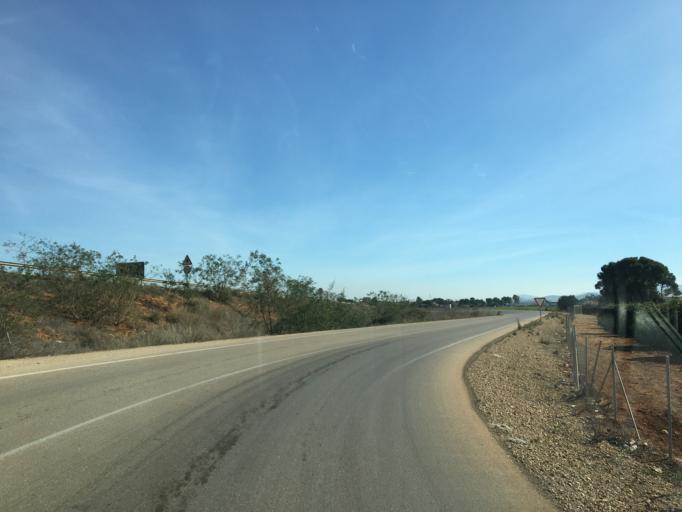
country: ES
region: Murcia
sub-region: Murcia
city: Cartagena
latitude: 37.6632
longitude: -1.0238
